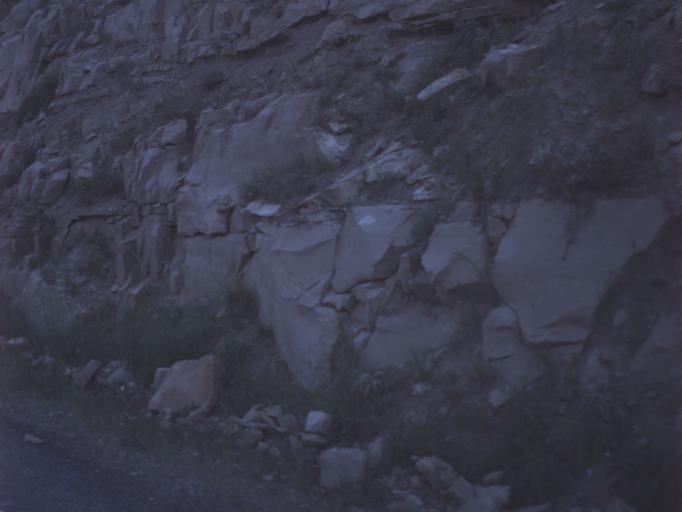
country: US
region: Utah
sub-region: Sanpete County
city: Fairview
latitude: 39.5862
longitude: -111.1928
